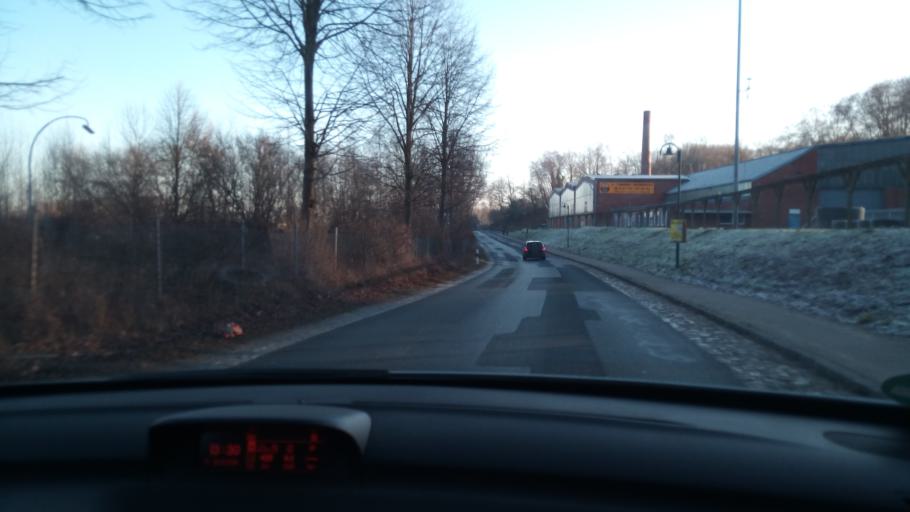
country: DE
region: Schleswig-Holstein
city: Buchhorst
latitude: 53.3810
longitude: 10.5721
